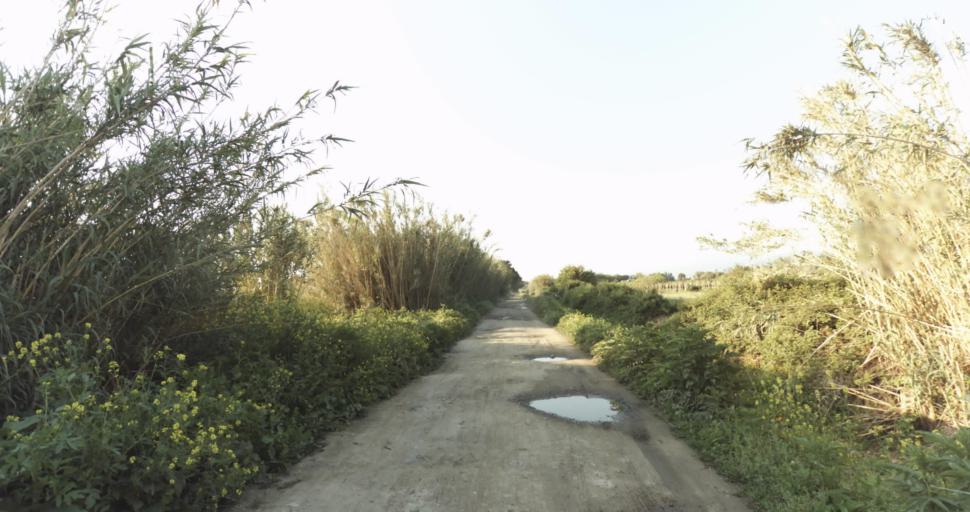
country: FR
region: Corsica
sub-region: Departement de la Haute-Corse
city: Biguglia
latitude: 42.6141
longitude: 9.4460
